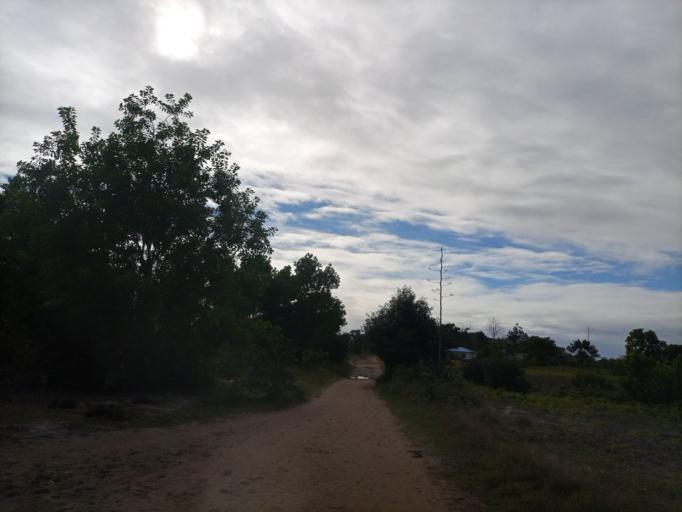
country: MG
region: Anosy
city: Fort Dauphin
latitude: -24.7799
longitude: 47.1805
